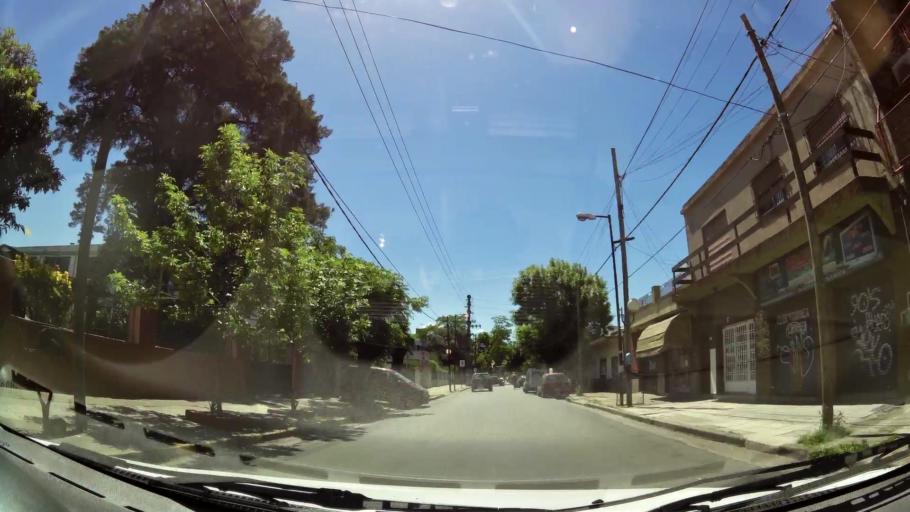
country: AR
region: Buenos Aires
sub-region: Partido de San Isidro
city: San Isidro
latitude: -34.5031
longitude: -58.5743
